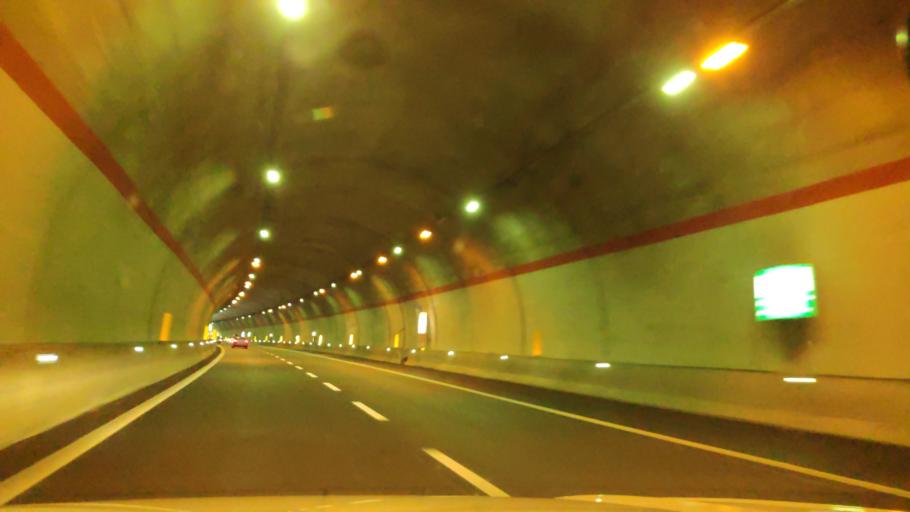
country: IT
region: Calabria
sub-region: Provincia di Cosenza
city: Morano Calabro
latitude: 39.8870
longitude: 16.1366
